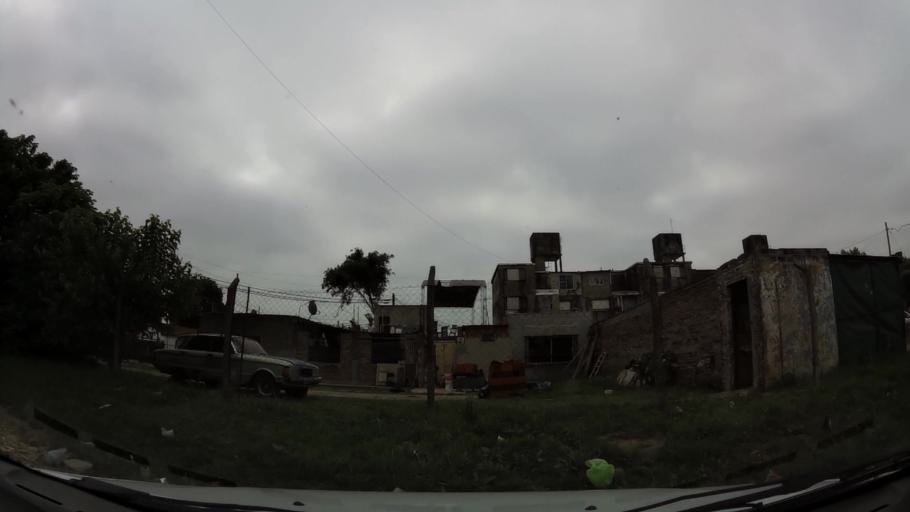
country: AR
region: Buenos Aires
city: San Justo
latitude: -34.7059
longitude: -58.5373
